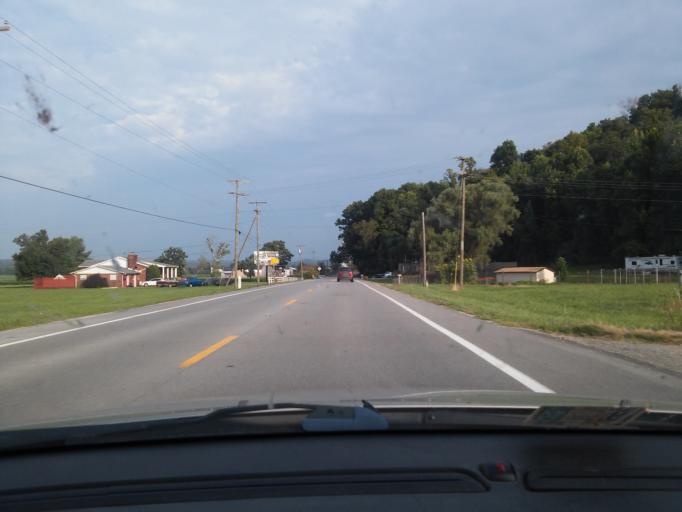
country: US
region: West Virginia
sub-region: Putnam County
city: Buffalo
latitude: 38.7561
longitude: -81.9911
